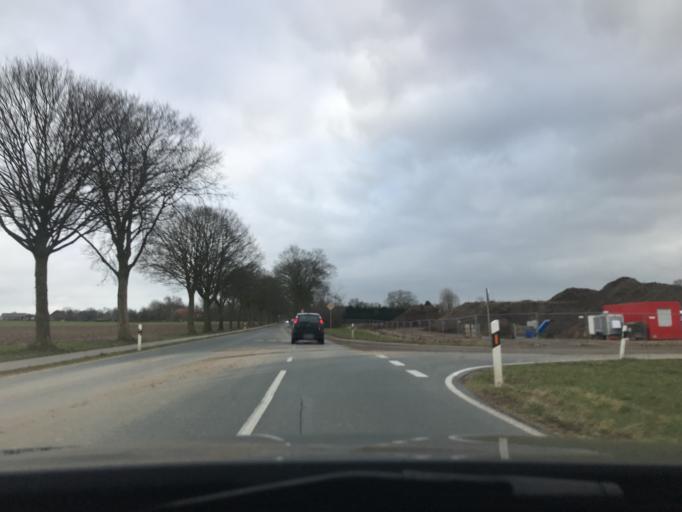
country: DE
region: North Rhine-Westphalia
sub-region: Regierungsbezirk Dusseldorf
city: Kleve
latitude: 51.7457
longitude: 6.1946
